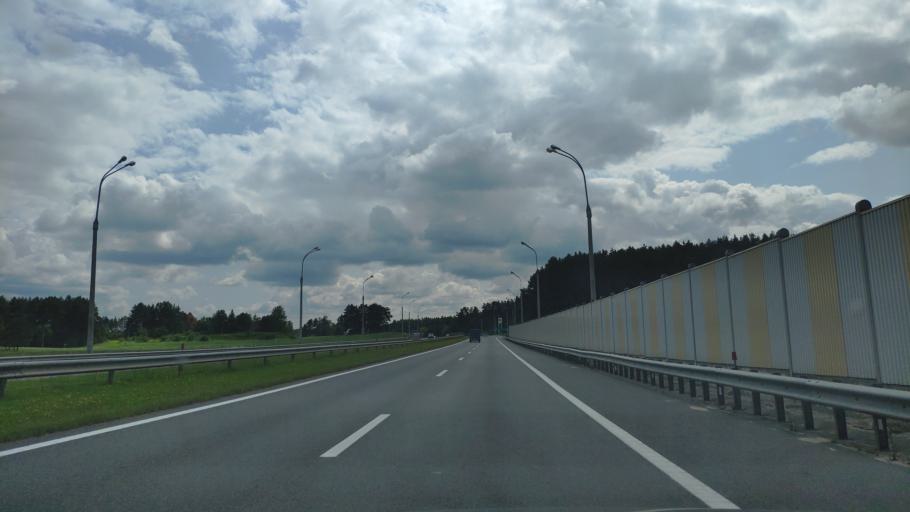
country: BY
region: Minsk
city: Zaslawye
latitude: 53.9958
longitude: 27.3061
